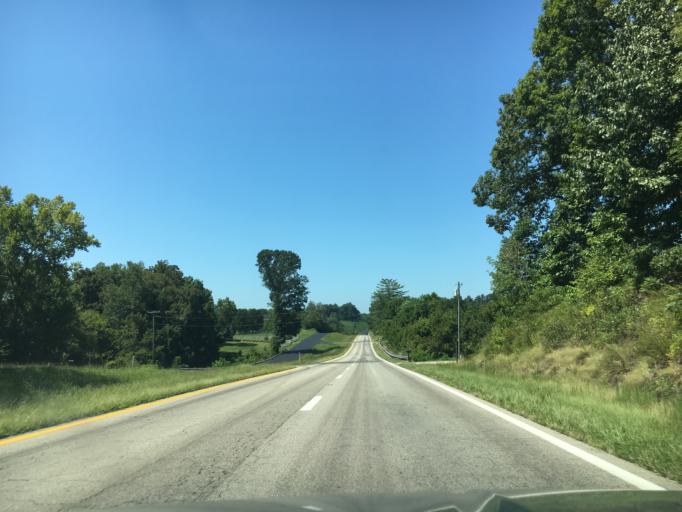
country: US
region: Virginia
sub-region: City of Danville
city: Danville
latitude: 36.5811
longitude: -79.2152
